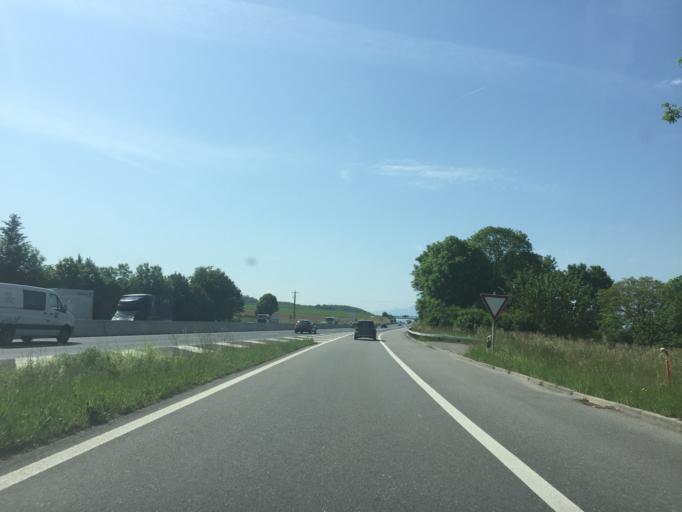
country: CH
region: Vaud
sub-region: Gros-de-Vaud District
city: Penthalaz
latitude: 46.5961
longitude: 6.5534
